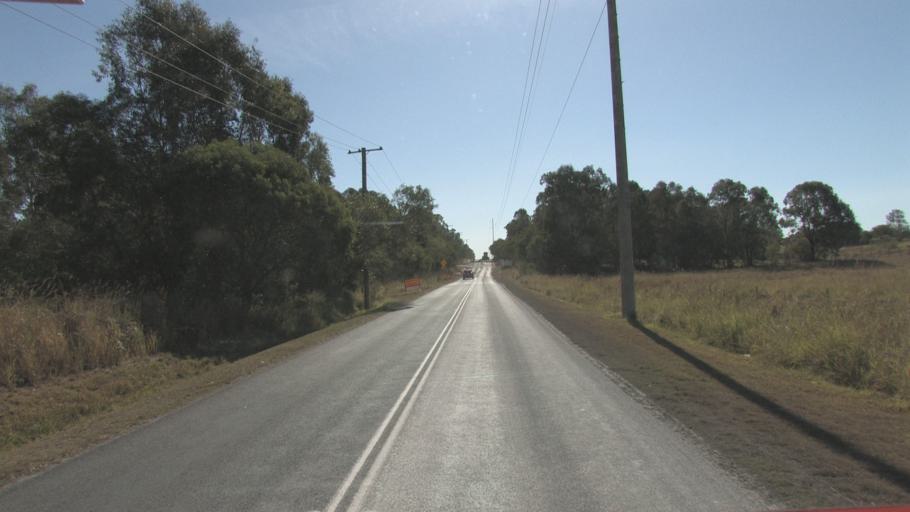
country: AU
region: Queensland
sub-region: Logan
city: Cedar Vale
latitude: -27.8595
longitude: 153.0194
